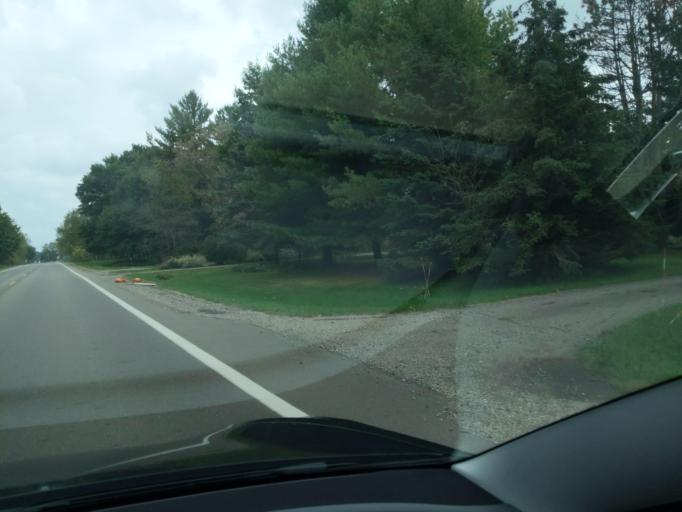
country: US
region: Michigan
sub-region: Eaton County
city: Eaton Rapids
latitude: 42.5353
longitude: -84.7248
